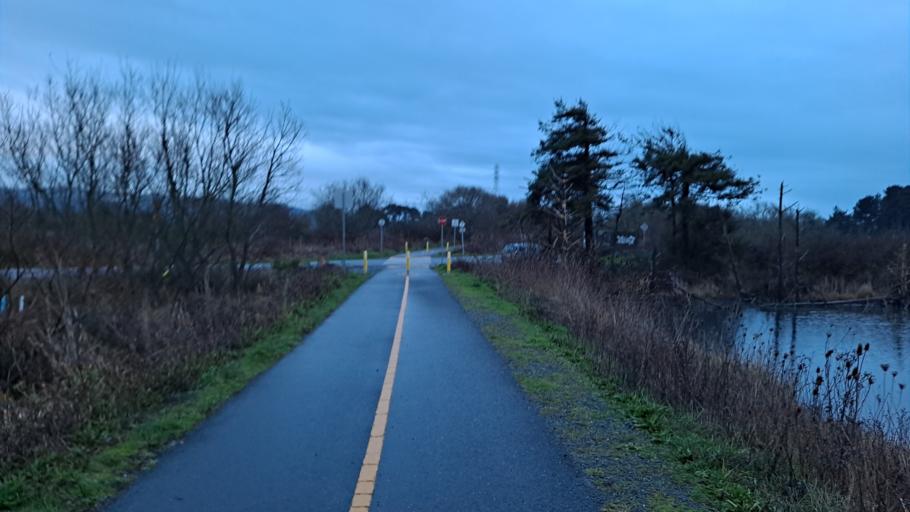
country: US
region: California
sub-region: Humboldt County
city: Arcata
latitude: 40.8614
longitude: -124.0933
